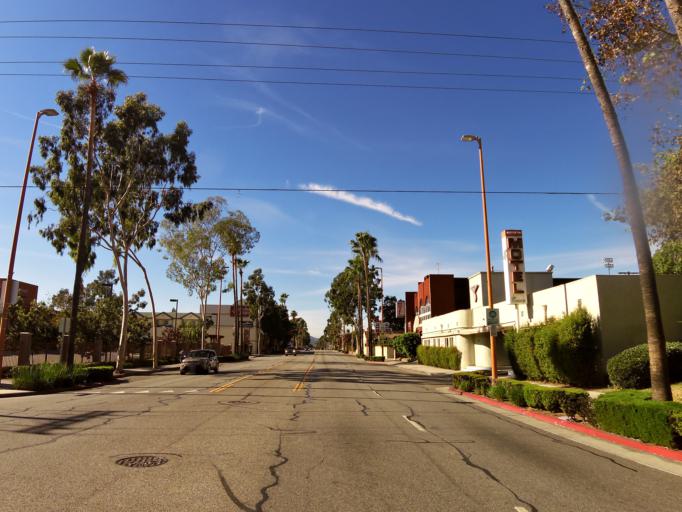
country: US
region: California
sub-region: Los Angeles County
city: Glendale
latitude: 34.1428
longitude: -118.2294
